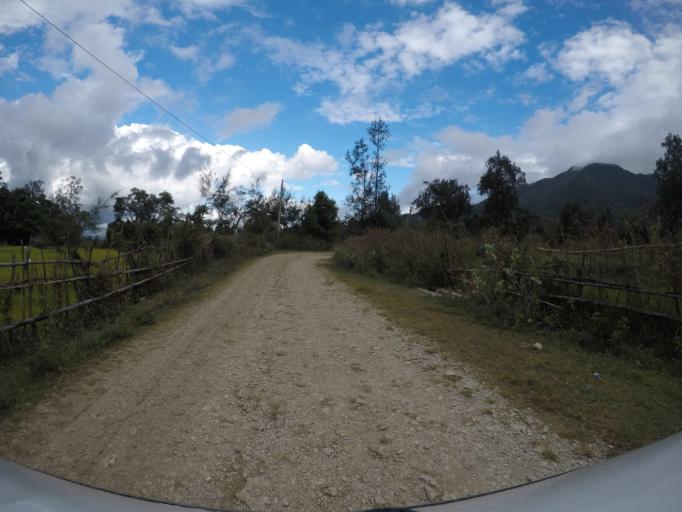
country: TL
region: Baucau
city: Venilale
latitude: -8.6785
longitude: 126.6353
